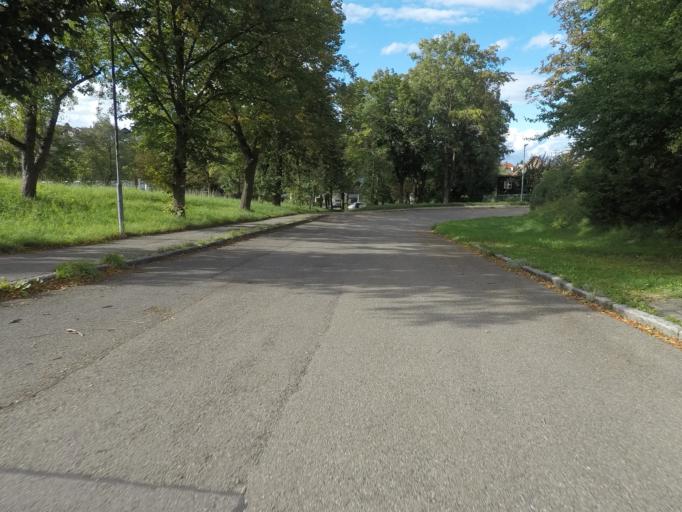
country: DE
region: Baden-Wuerttemberg
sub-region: Tuebingen Region
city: Pfullingen
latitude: 48.4558
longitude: 9.2200
